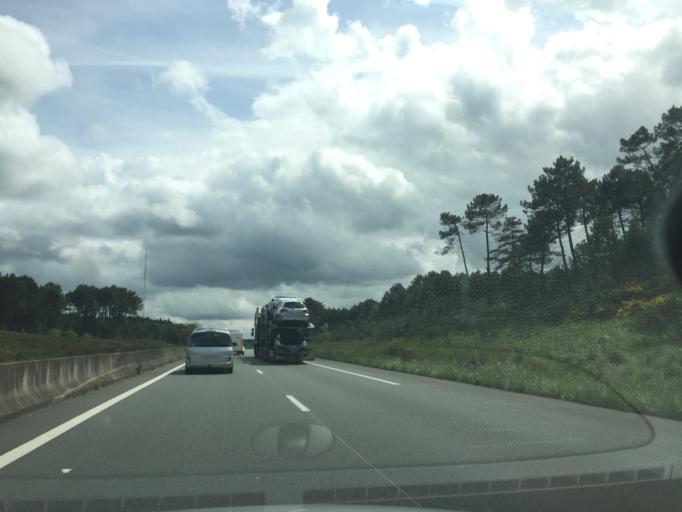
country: FR
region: Pays de la Loire
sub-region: Departement de la Sarthe
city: Mayet
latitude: 47.7825
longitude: 0.3100
